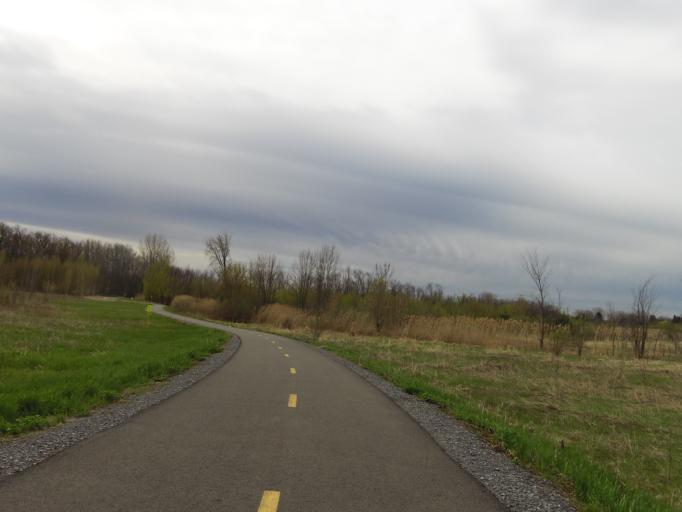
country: CA
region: Quebec
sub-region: Laurentides
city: Oka
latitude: 45.4722
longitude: -74.0664
